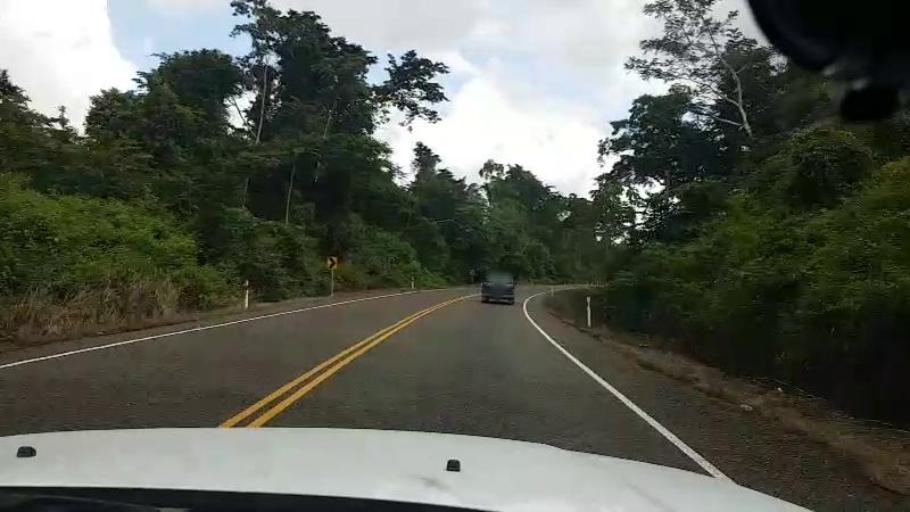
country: BZ
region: Cayo
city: Belmopan
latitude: 17.1540
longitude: -88.6750
